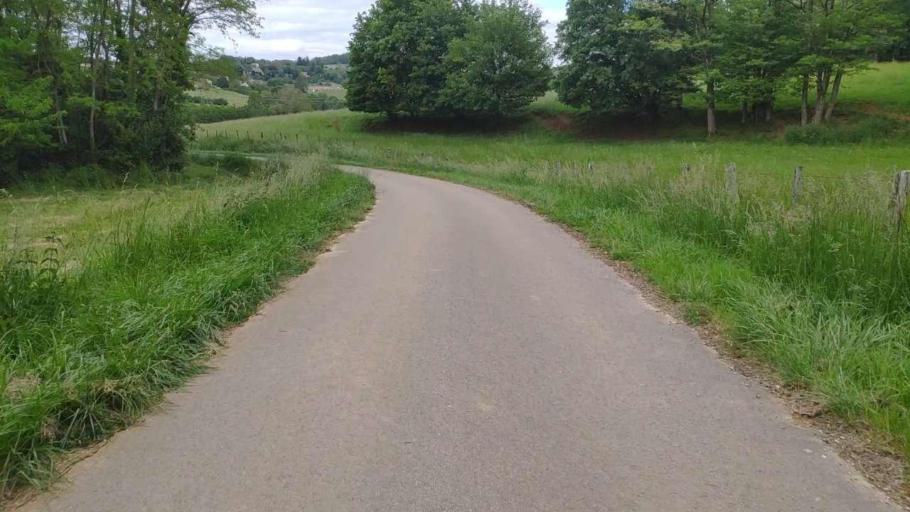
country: FR
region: Franche-Comte
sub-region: Departement du Jura
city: Bletterans
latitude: 46.7876
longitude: 5.5472
